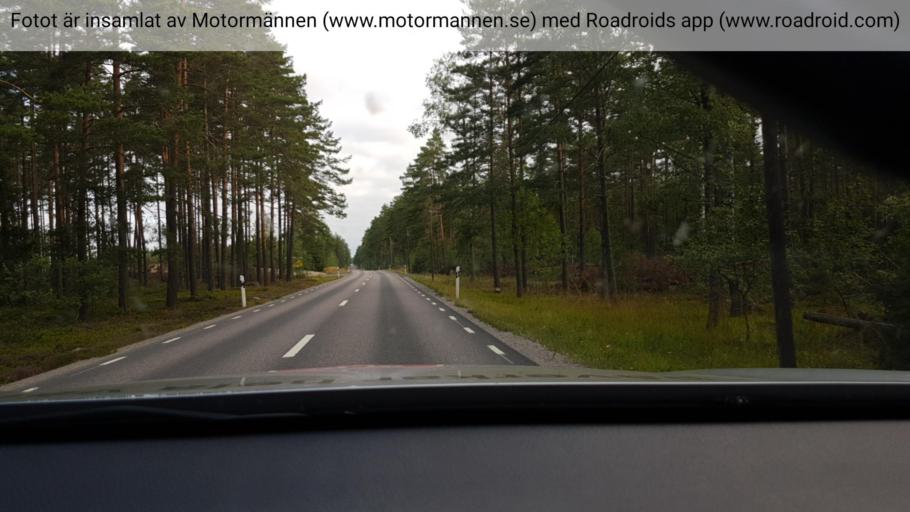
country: SE
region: Stockholm
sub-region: Norrtalje Kommun
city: Rimbo
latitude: 59.7855
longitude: 18.4378
